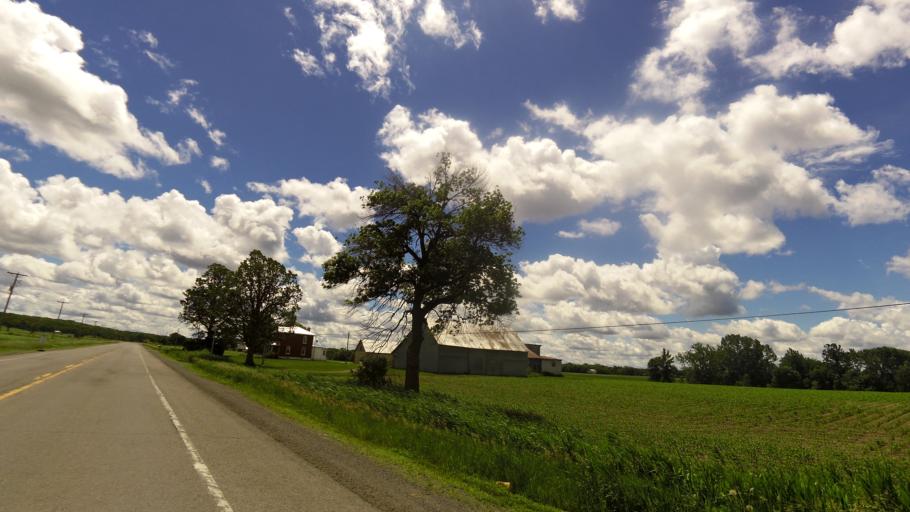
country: CA
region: Quebec
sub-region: Monteregie
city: Hudson
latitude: 45.5156
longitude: -74.1627
